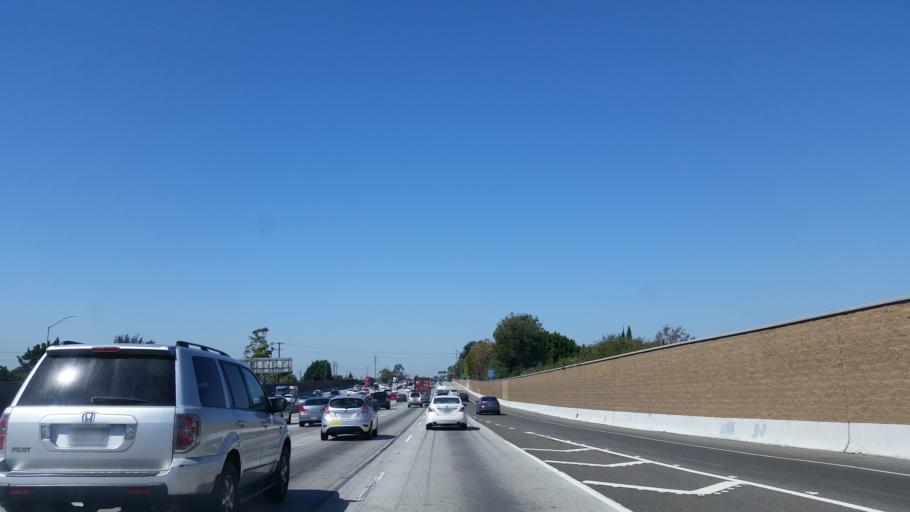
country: US
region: California
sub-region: Orange County
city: Rossmoor
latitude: 33.7920
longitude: -118.1011
